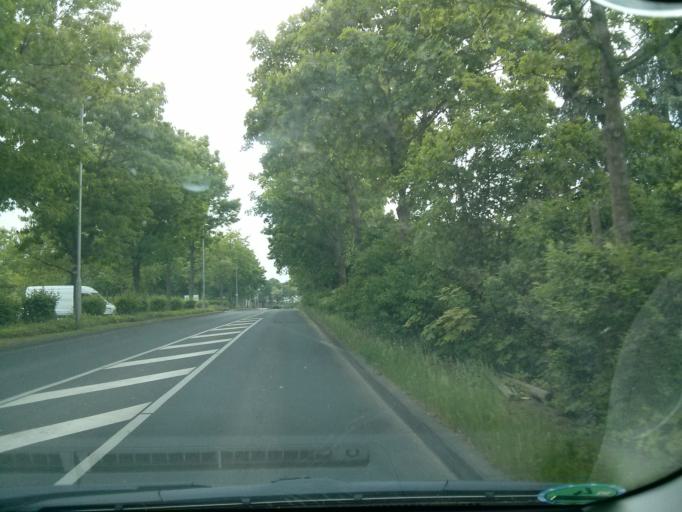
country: DE
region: North Rhine-Westphalia
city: Meckenheim
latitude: 50.6232
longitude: 7.0398
